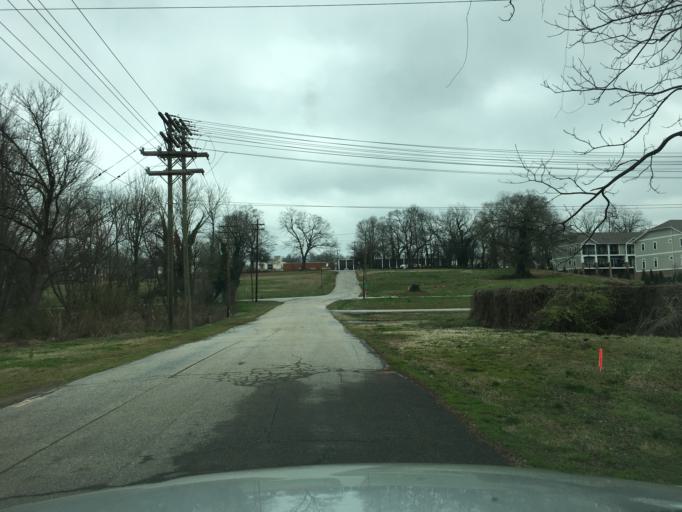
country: US
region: South Carolina
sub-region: Greenville County
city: Greenville
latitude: 34.8525
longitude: -82.4111
